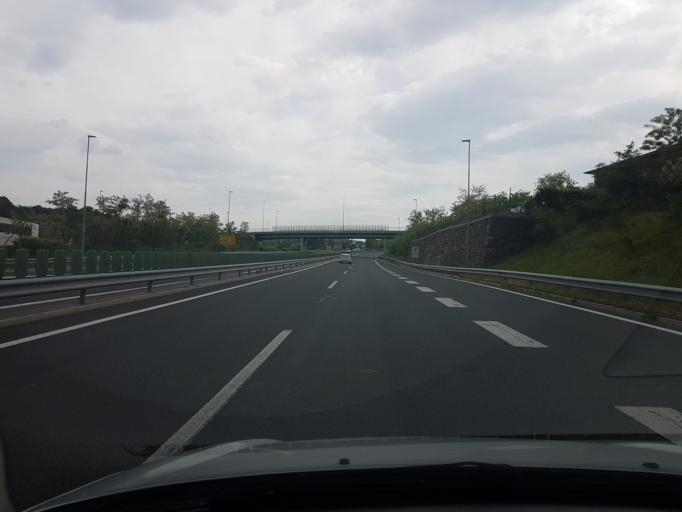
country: SI
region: Koper-Capodistria
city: Spodnje Skofije
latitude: 45.5787
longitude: 13.7963
